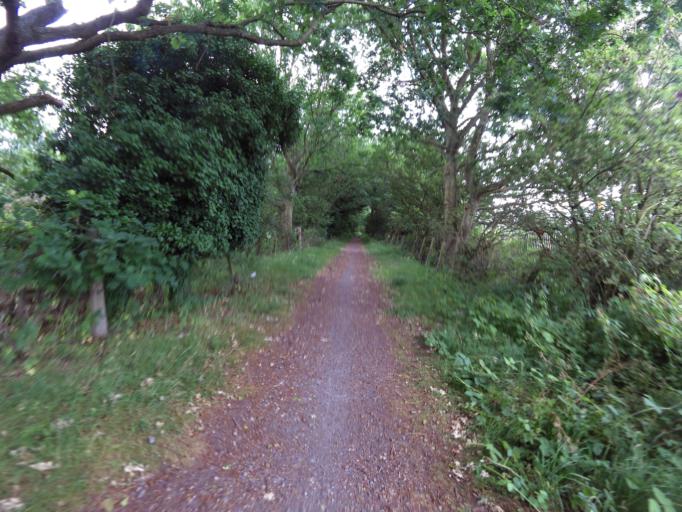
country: GB
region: England
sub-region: Norfolk
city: Ditchingham
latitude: 52.4712
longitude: 1.4669
